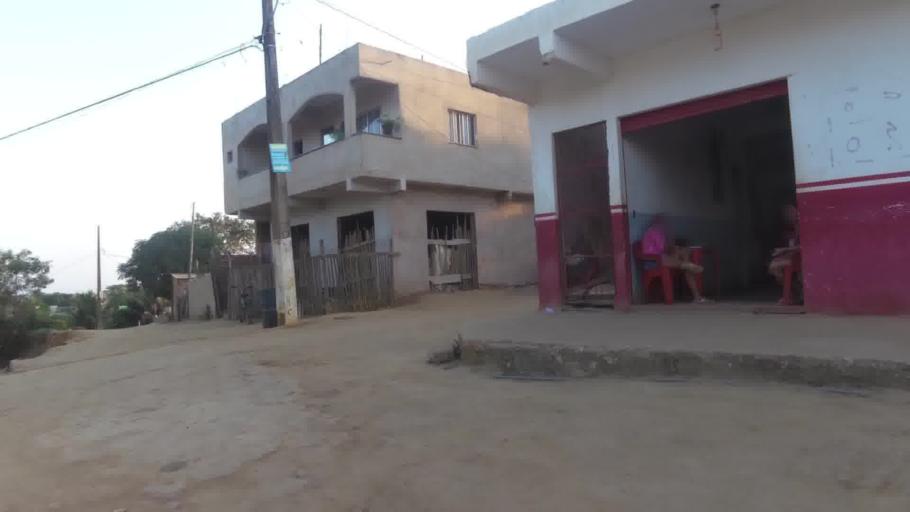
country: BR
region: Espirito Santo
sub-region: Piuma
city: Piuma
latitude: -20.8276
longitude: -40.7204
